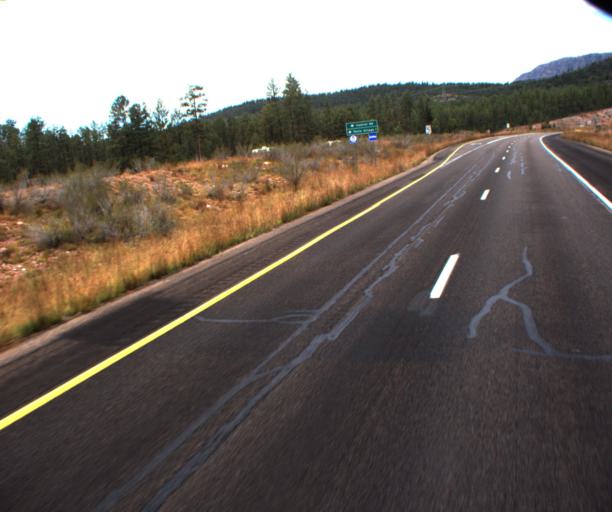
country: US
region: Arizona
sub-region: Gila County
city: Star Valley
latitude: 34.3153
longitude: -111.1132
